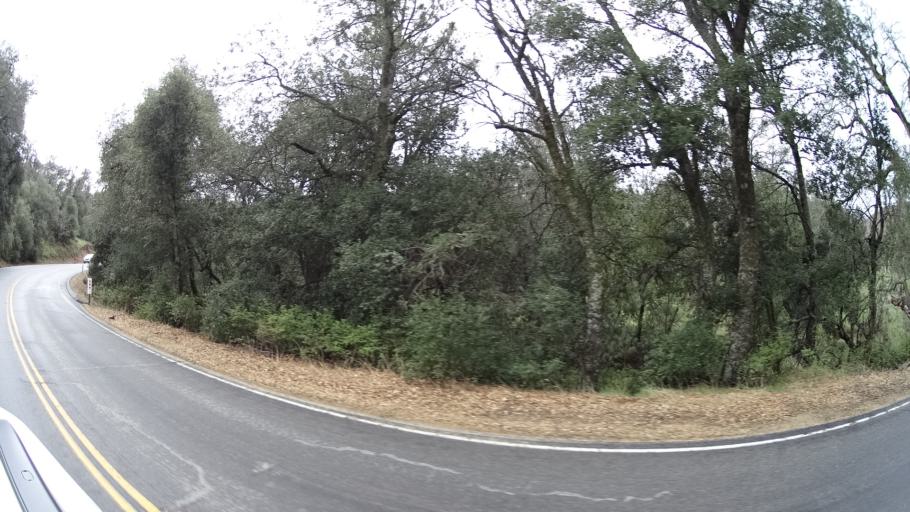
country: US
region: California
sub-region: San Diego County
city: Julian
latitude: 33.0897
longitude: -116.5950
